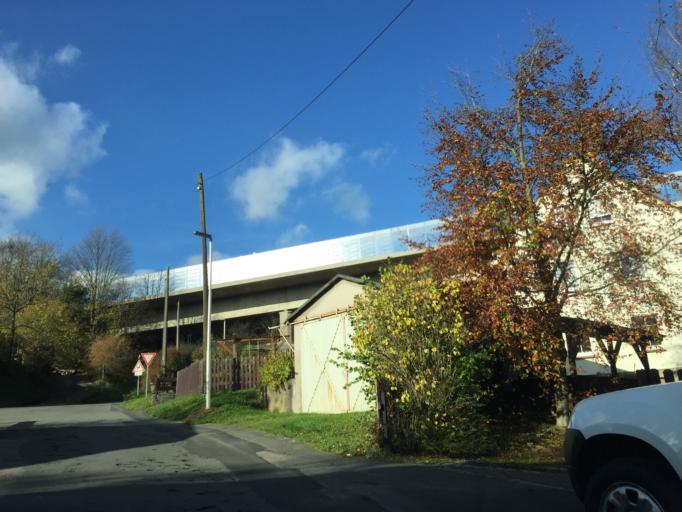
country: DE
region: North Rhine-Westphalia
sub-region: Regierungsbezirk Arnsberg
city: Nachrodt-Wiblingwerde
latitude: 51.3748
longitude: 7.6338
